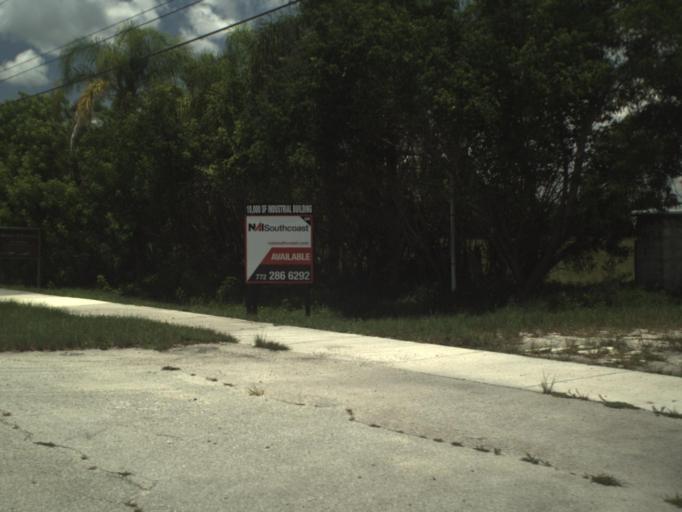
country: US
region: Florida
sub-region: Martin County
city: Port Salerno
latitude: 27.1260
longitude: -80.2271
